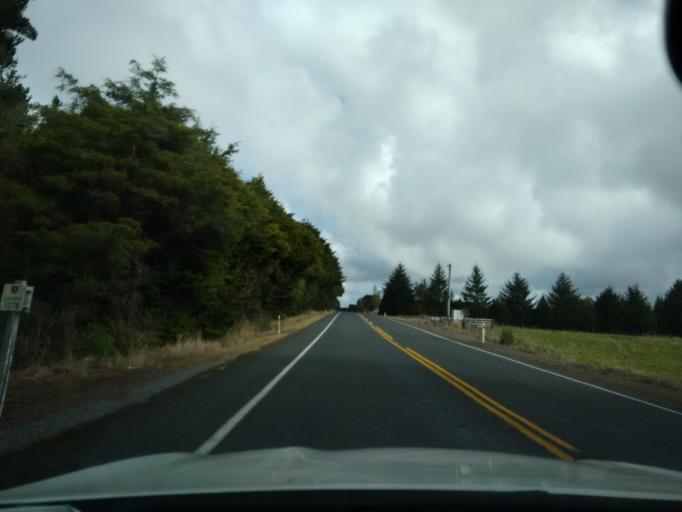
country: NZ
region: Manawatu-Wanganui
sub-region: Ruapehu District
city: Waiouru
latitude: -39.2863
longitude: 175.3869
